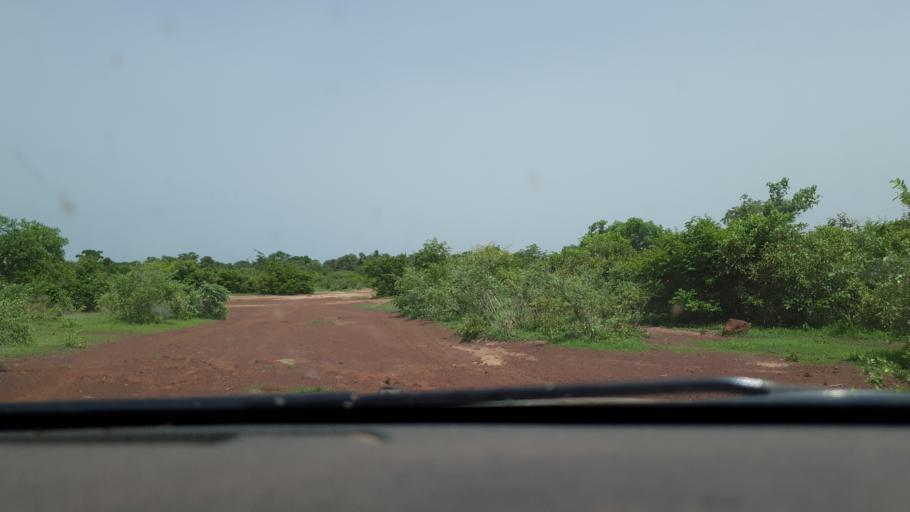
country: ML
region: Koulikoro
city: Koulikoro
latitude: 12.6667
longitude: -7.2377
